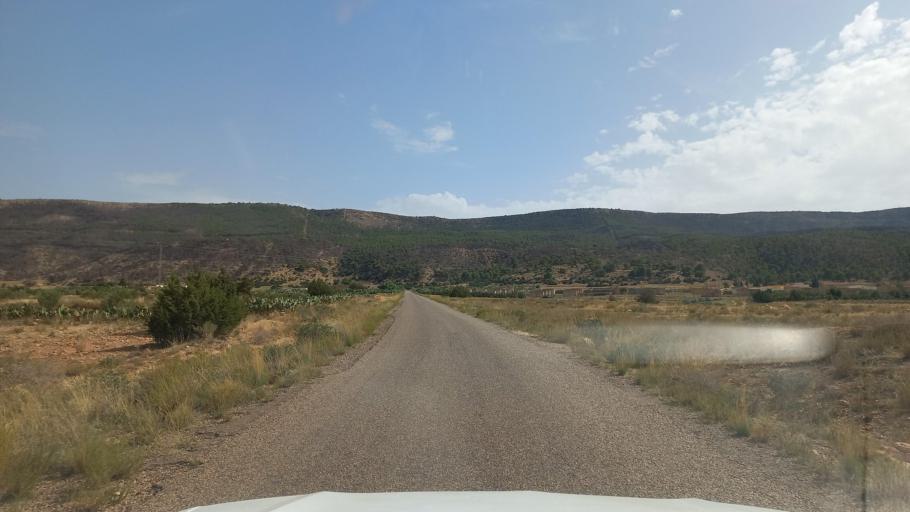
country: TN
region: Al Qasrayn
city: Kasserine
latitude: 35.3584
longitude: 8.8857
